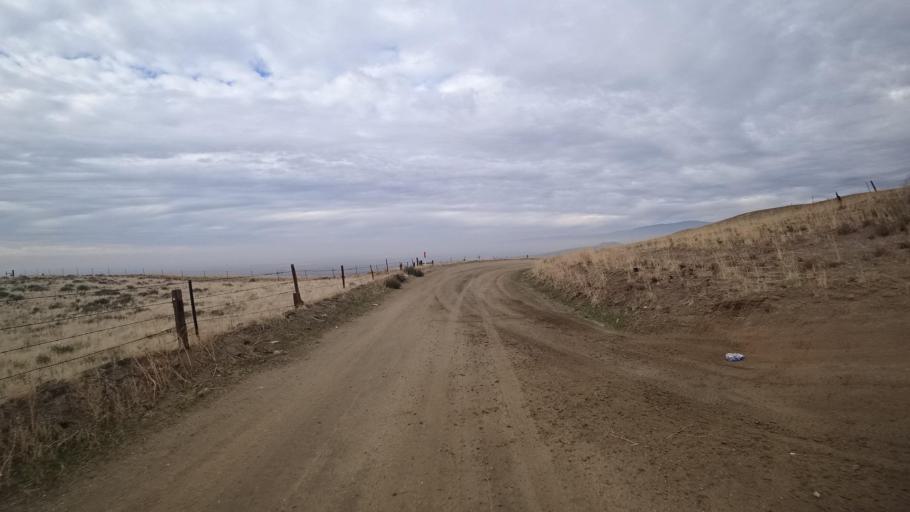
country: US
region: California
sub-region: Kern County
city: Arvin
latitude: 35.1366
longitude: -118.7955
